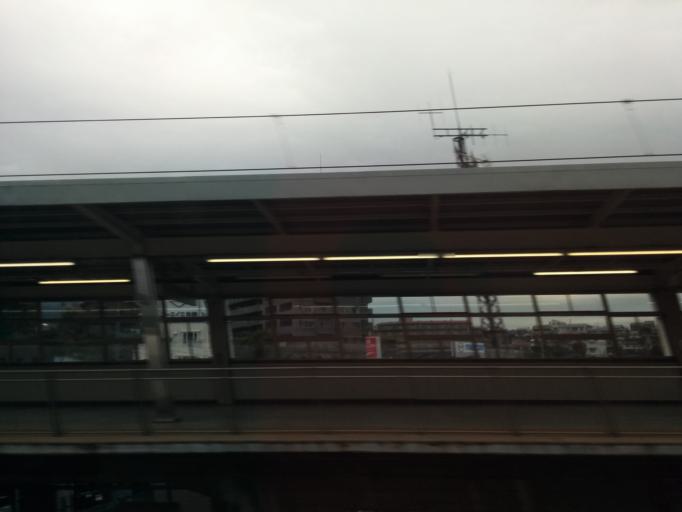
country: JP
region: Kanagawa
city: Odawara
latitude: 35.2571
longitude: 139.1555
